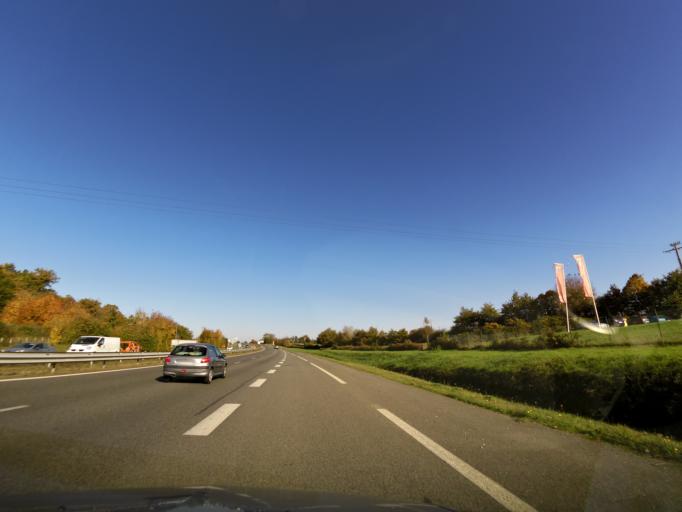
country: FR
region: Brittany
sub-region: Departement d'Ille-et-Vilaine
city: Pance
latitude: 47.8953
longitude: -1.6869
